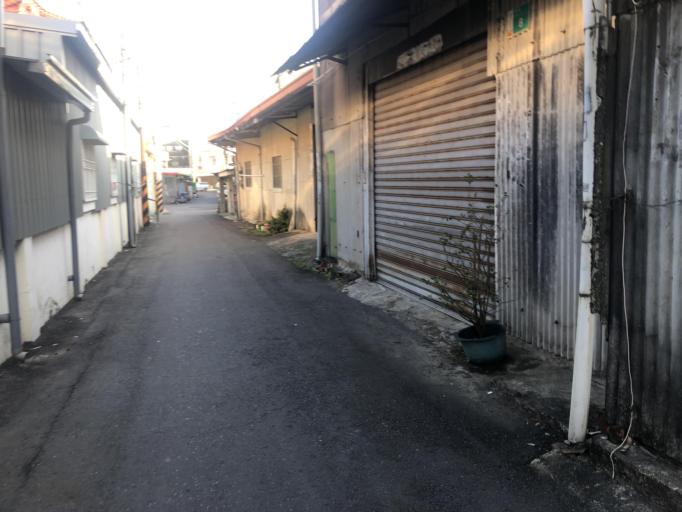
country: TW
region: Taiwan
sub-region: Tainan
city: Tainan
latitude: 23.0407
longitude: 120.1837
